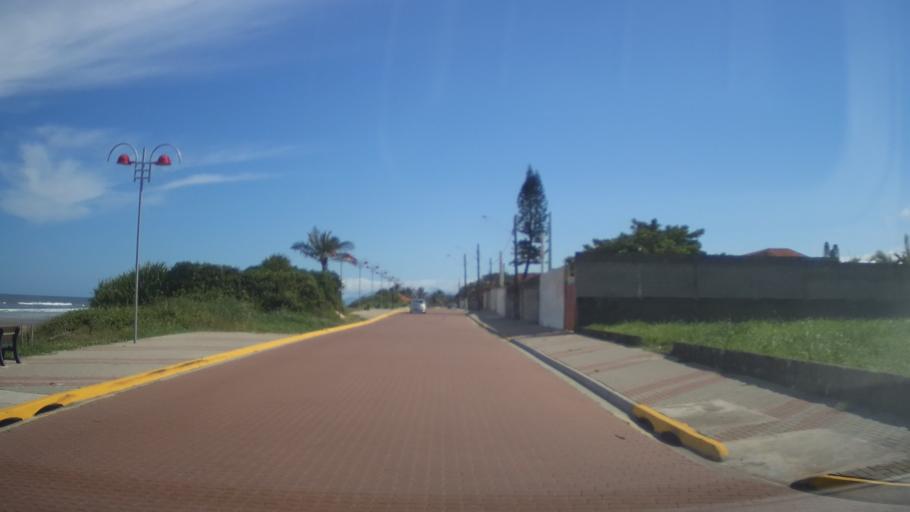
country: BR
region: Sao Paulo
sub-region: Itanhaem
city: Itanhaem
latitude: -24.1684
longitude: -46.7547
